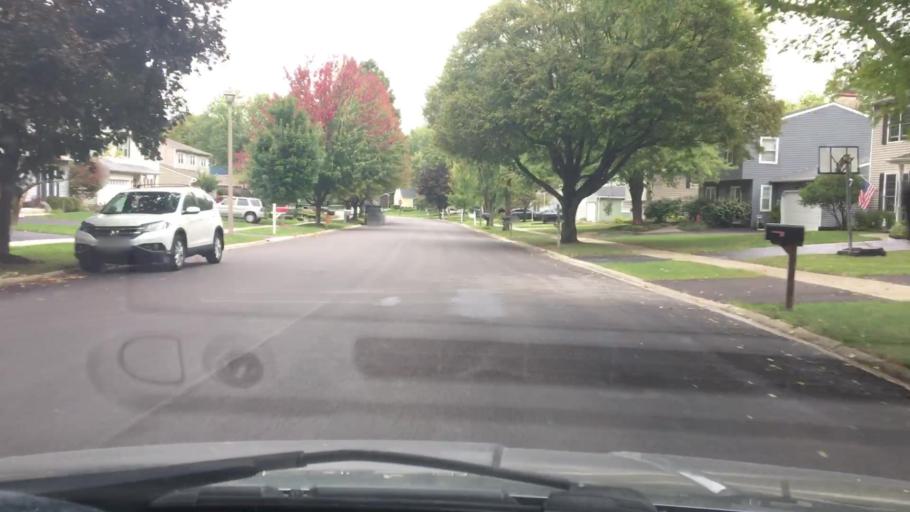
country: US
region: Illinois
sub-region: DuPage County
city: Naperville
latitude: 41.7397
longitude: -88.1357
